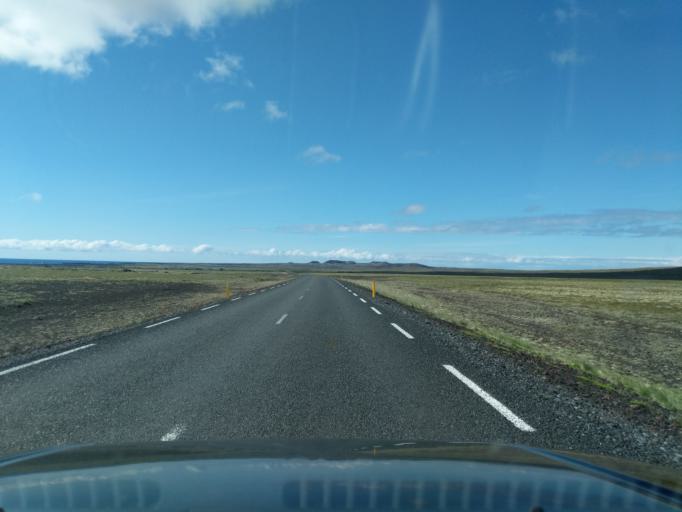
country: IS
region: West
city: Olafsvik
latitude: 64.7992
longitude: -23.9249
